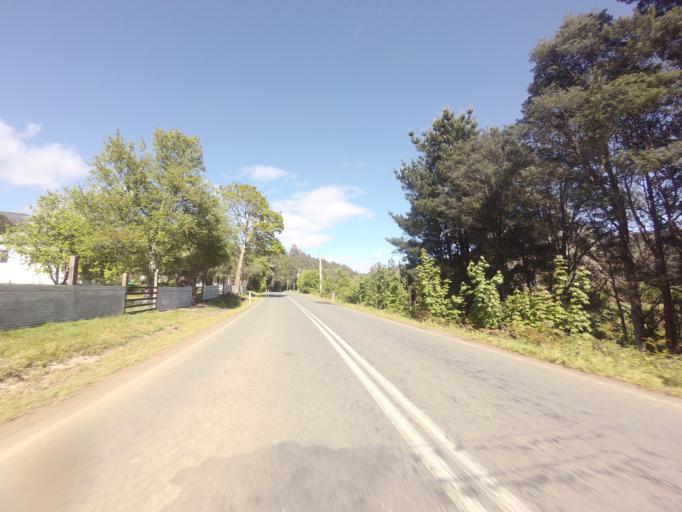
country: AU
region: Tasmania
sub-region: Derwent Valley
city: New Norfolk
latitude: -42.7119
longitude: 146.7036
